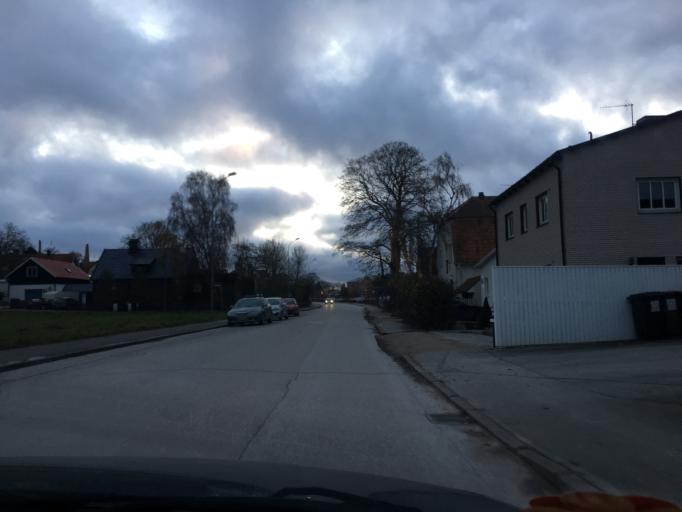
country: SE
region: Gotland
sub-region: Gotland
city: Visby
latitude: 57.6506
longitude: 18.3049
